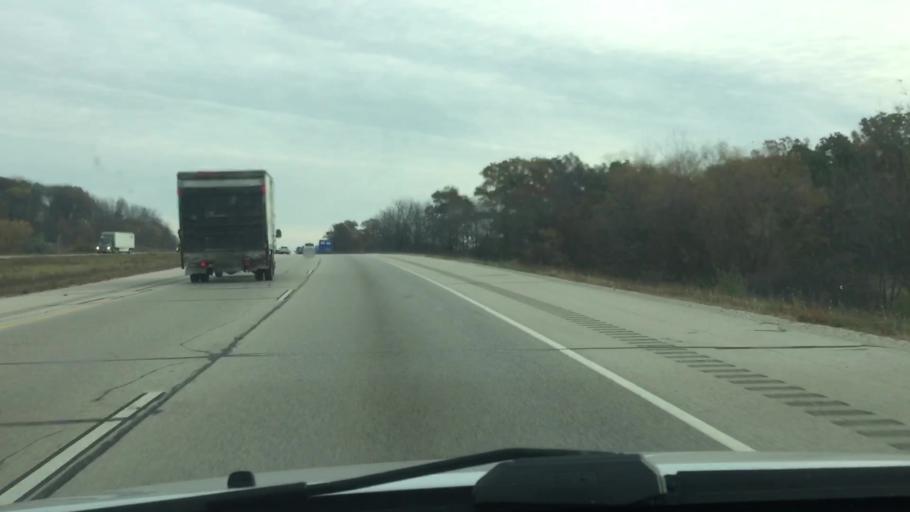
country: US
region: Wisconsin
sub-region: Waukesha County
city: Muskego
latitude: 42.9417
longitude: -88.1258
